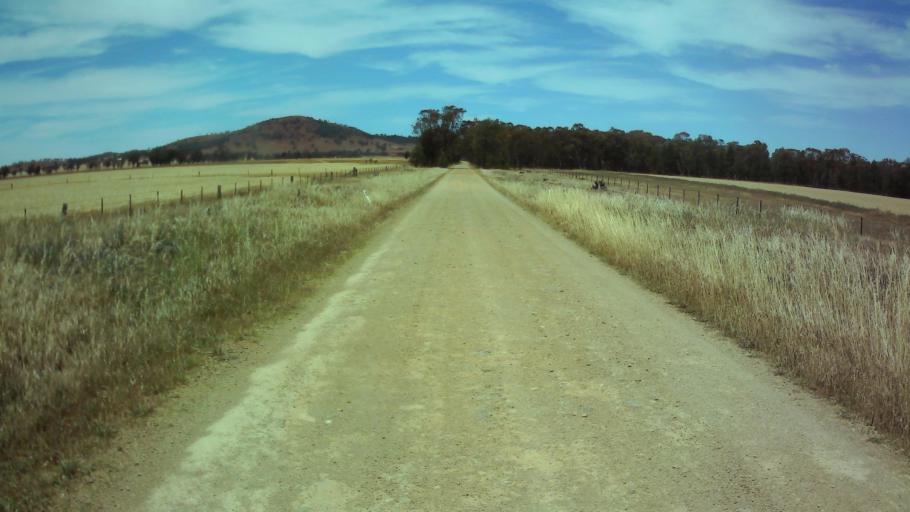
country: AU
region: New South Wales
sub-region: Weddin
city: Grenfell
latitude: -33.7612
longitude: 148.1200
